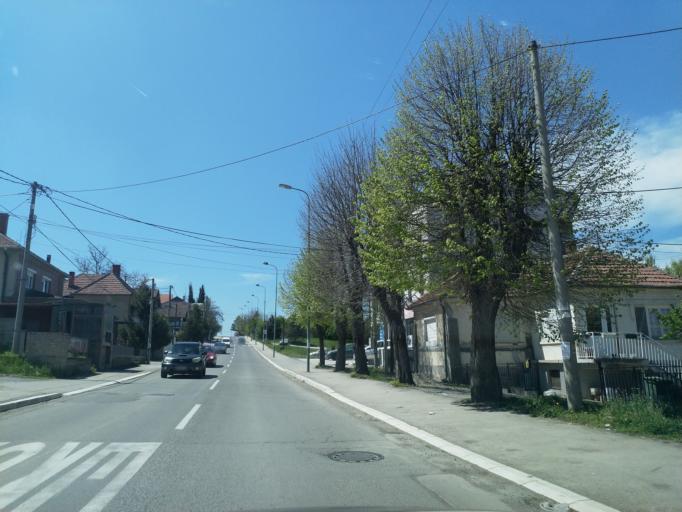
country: RS
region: Central Serbia
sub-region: Belgrade
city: Lazarevac
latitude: 44.3778
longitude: 20.2594
